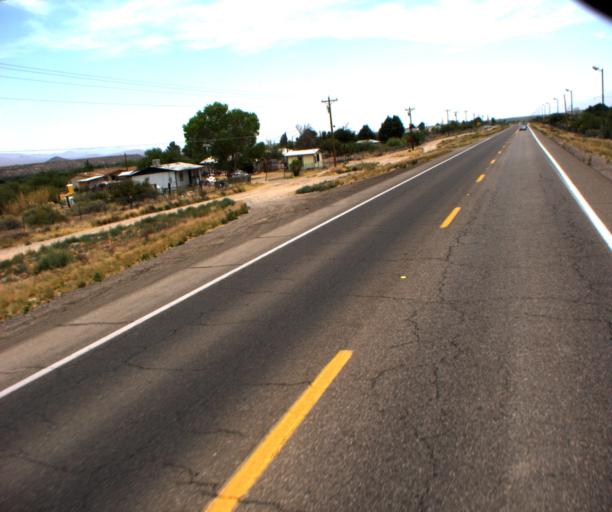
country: US
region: Arizona
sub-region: Graham County
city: Bylas
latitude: 33.1299
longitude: -110.1184
